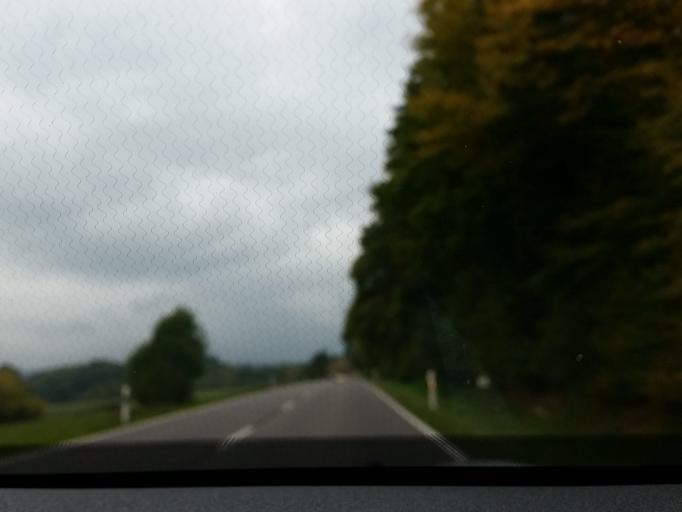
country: DE
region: Saarland
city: Weiskirchen
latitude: 49.5143
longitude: 6.8268
